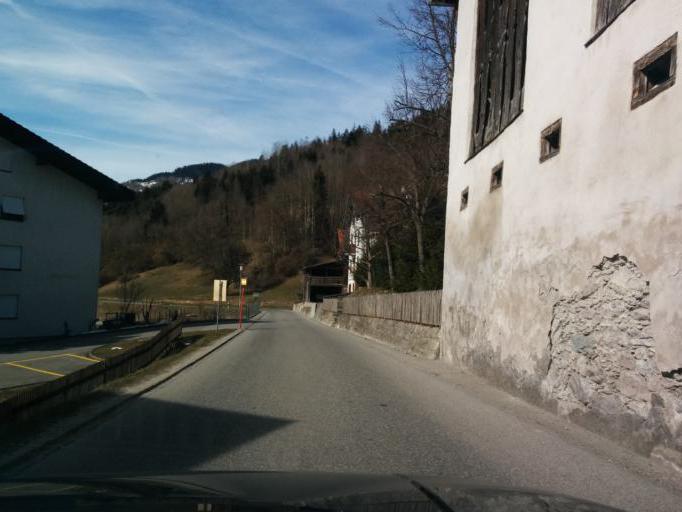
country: CH
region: Grisons
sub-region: Surselva District
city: Laax
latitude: 46.7911
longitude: 9.2558
